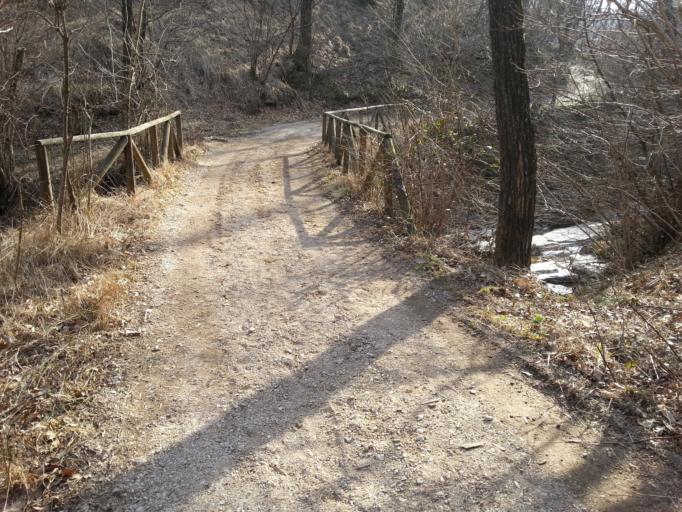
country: IT
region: Lombardy
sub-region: Provincia di Como
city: Albavilla
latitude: 45.8101
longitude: 9.1807
